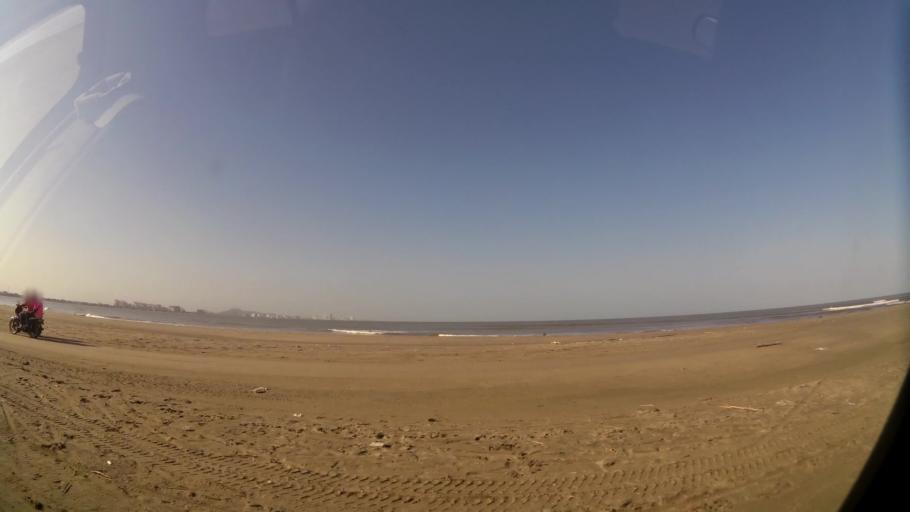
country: CO
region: Bolivar
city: Cartagena
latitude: 10.4944
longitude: -75.4968
